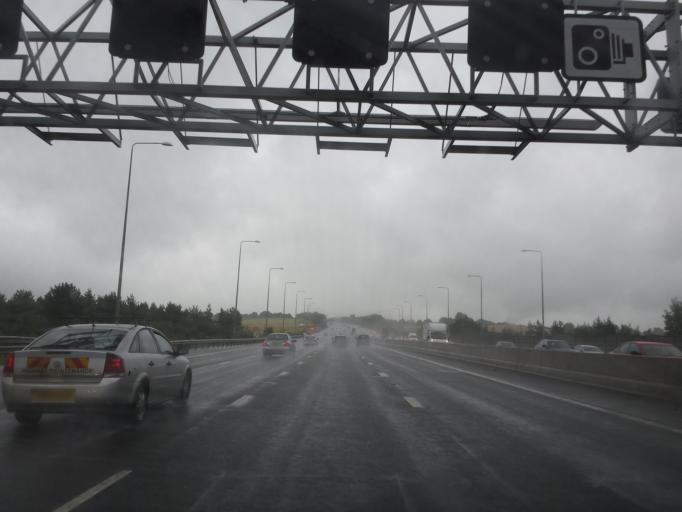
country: GB
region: England
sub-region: Derbyshire
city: Pinxton
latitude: 53.0897
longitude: -1.3048
